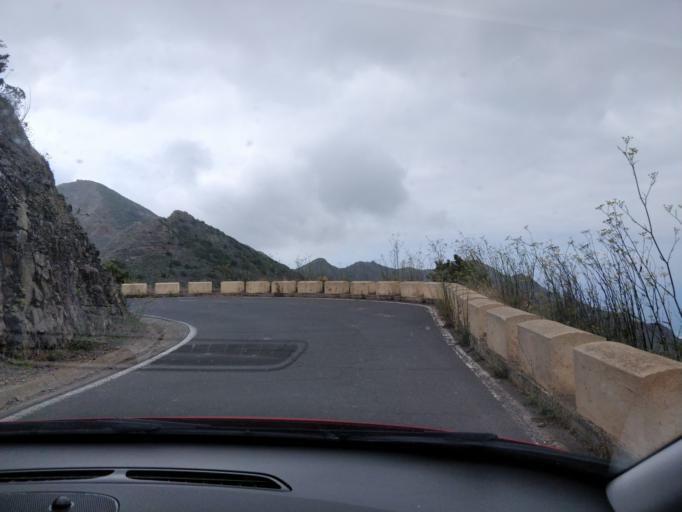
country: ES
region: Canary Islands
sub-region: Provincia de Santa Cruz de Tenerife
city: Tanque
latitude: 28.3267
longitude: -16.8547
